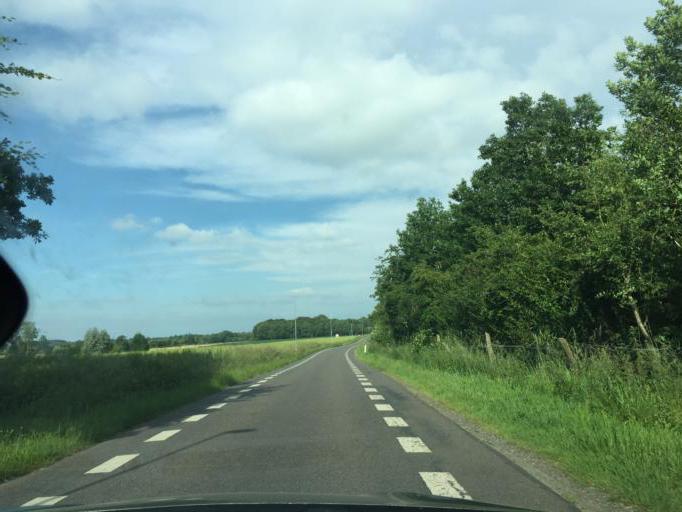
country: DK
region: South Denmark
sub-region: Faaborg-Midtfyn Kommune
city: Arslev
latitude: 55.3111
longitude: 10.5085
